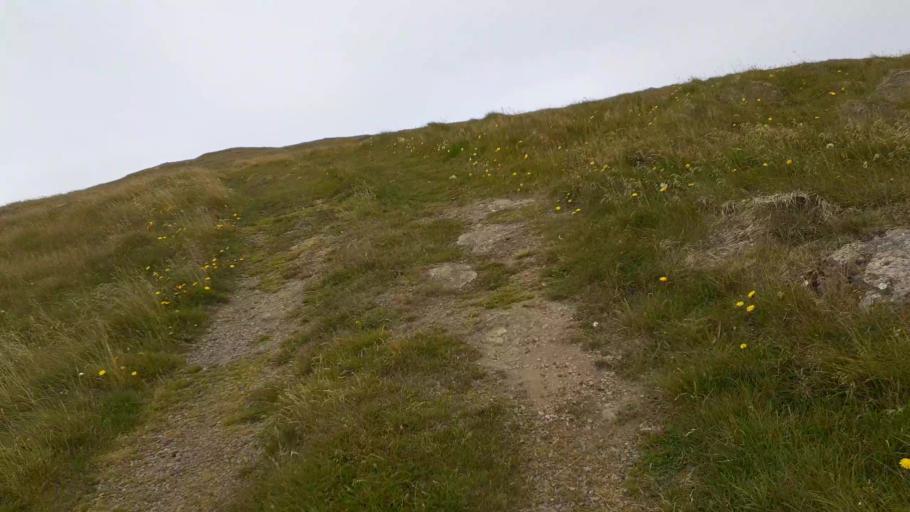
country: IS
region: Northeast
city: Dalvik
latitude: 66.5335
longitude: -17.9826
